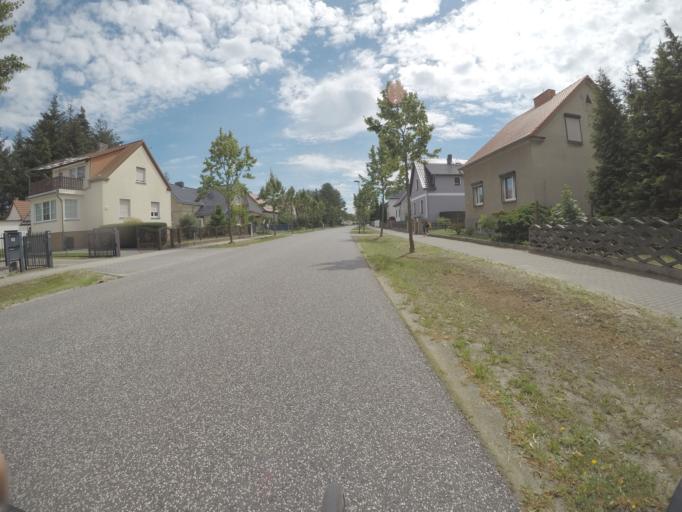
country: DE
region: Brandenburg
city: Storkow
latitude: 52.2508
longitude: 13.9406
